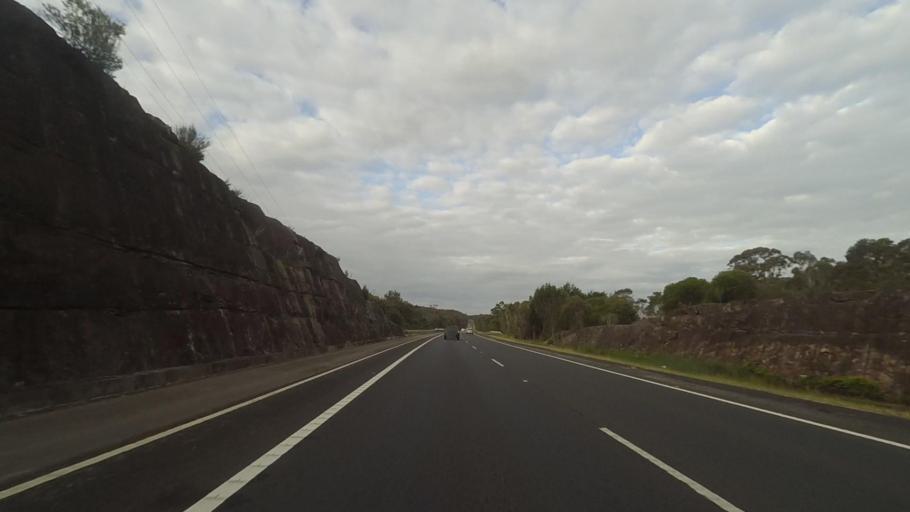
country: AU
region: New South Wales
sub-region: Wollongong
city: Helensburgh
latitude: -34.1874
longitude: 150.9685
